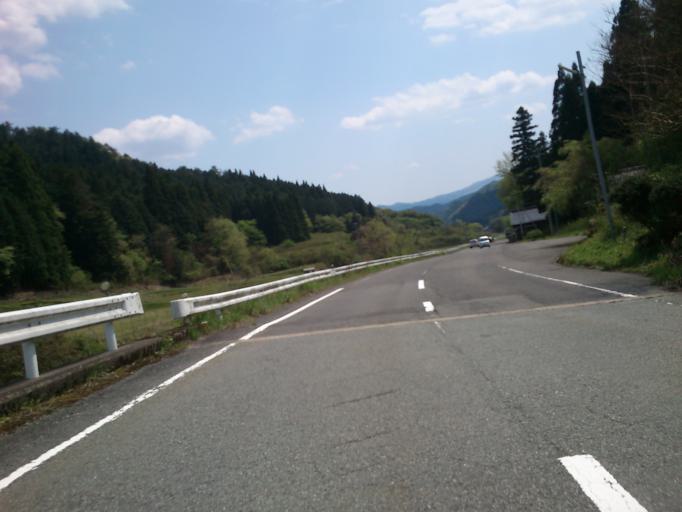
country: JP
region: Kyoto
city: Fukuchiyama
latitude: 35.3823
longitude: 134.9396
